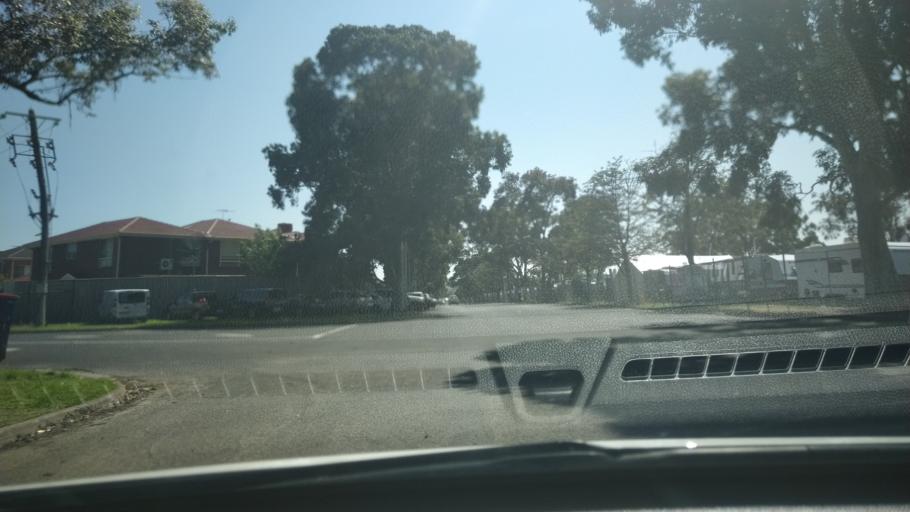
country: AU
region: Victoria
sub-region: Greater Dandenong
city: Springvale
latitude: -37.9525
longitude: 145.1617
